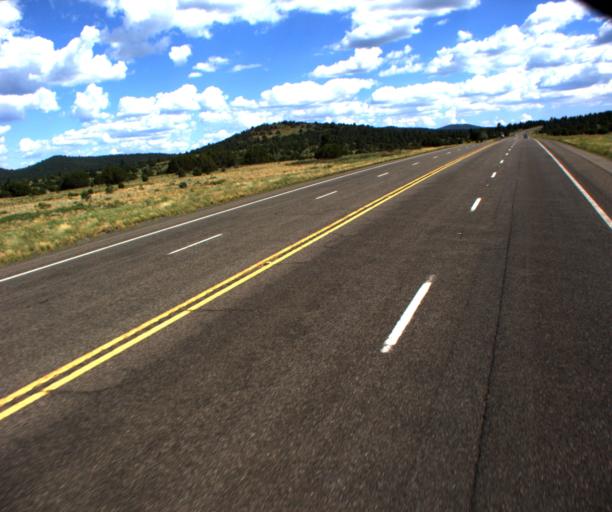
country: US
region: Arizona
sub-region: Coconino County
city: Williams
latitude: 35.3092
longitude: -112.1460
